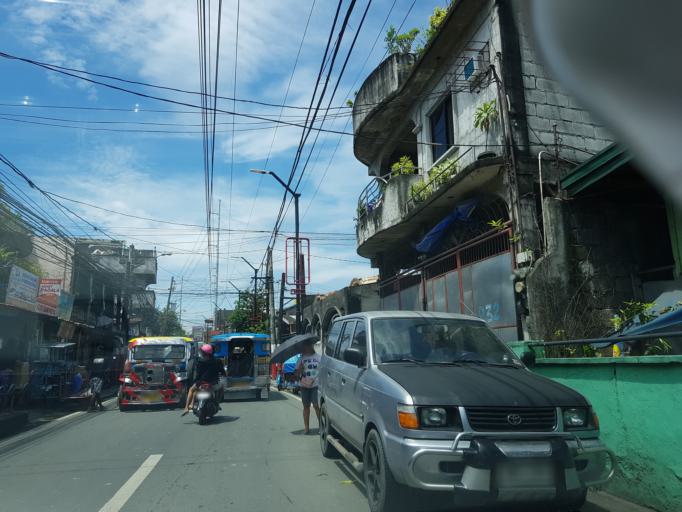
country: PH
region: Calabarzon
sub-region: Province of Rizal
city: Taguig
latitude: 14.5100
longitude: 121.0675
